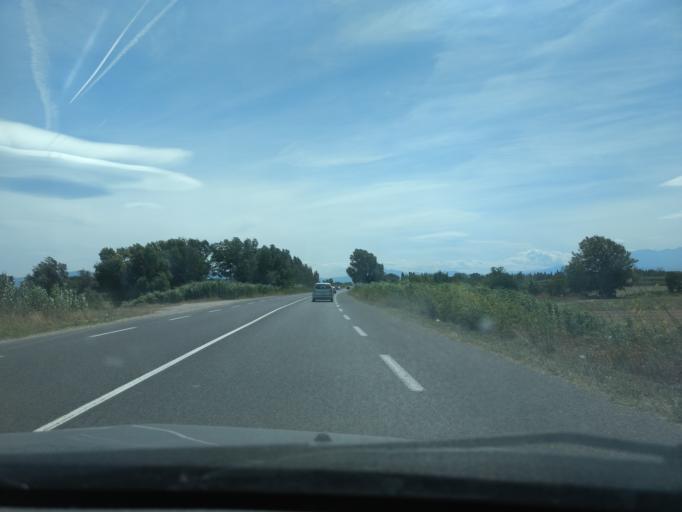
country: FR
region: Languedoc-Roussillon
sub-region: Departement des Pyrenees-Orientales
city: Sainte-Marie-Plage
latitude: 42.7153
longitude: 3.0272
